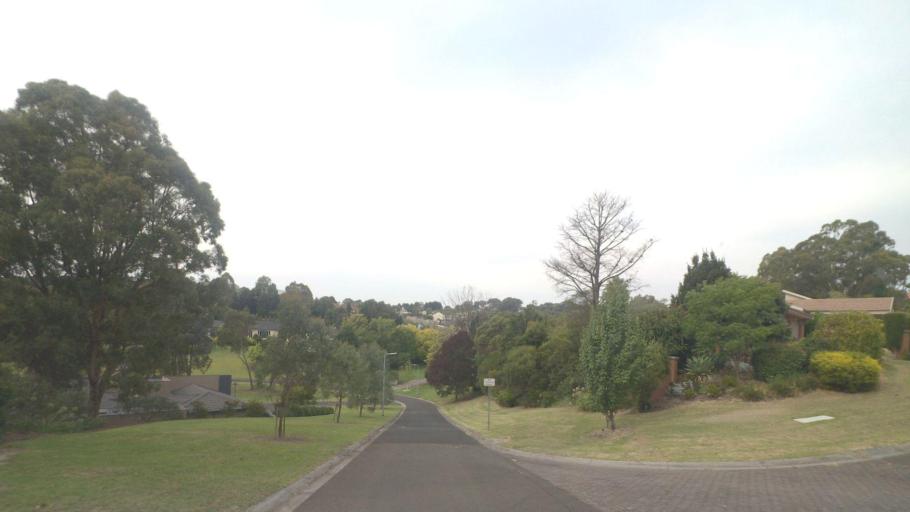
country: AU
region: Victoria
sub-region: Manningham
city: Park Orchards
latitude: -37.7642
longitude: 145.1908
